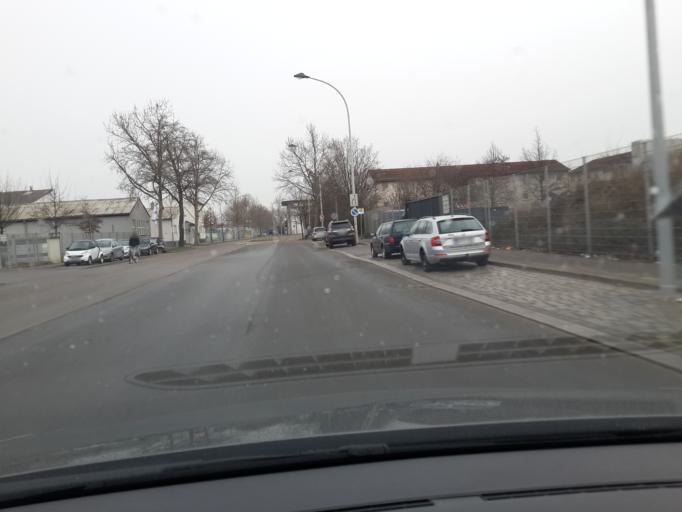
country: DE
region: Baden-Wuerttemberg
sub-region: Regierungsbezirk Stuttgart
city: Neckarsulm
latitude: 49.1755
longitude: 9.2178
